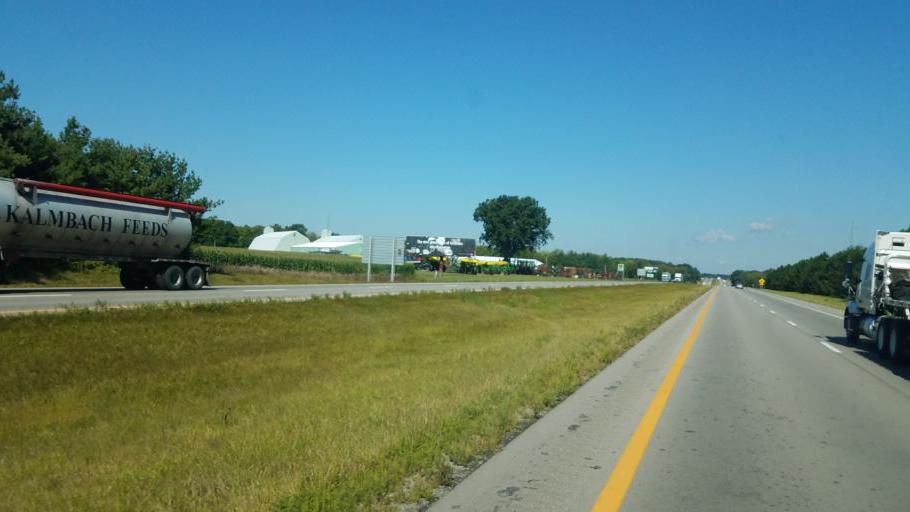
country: US
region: Ohio
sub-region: Wyandot County
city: Upper Sandusky
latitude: 40.8429
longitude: -83.2513
